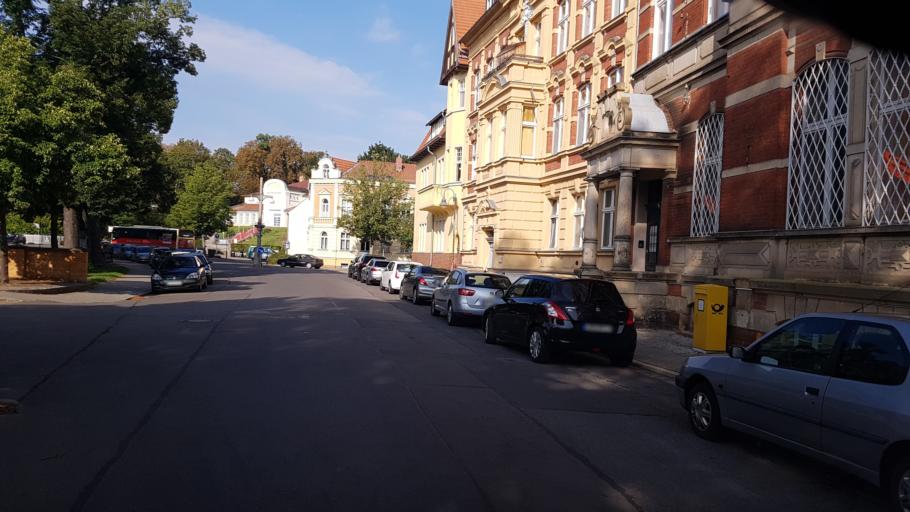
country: DE
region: Brandenburg
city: Luckau
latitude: 51.8541
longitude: 13.7155
